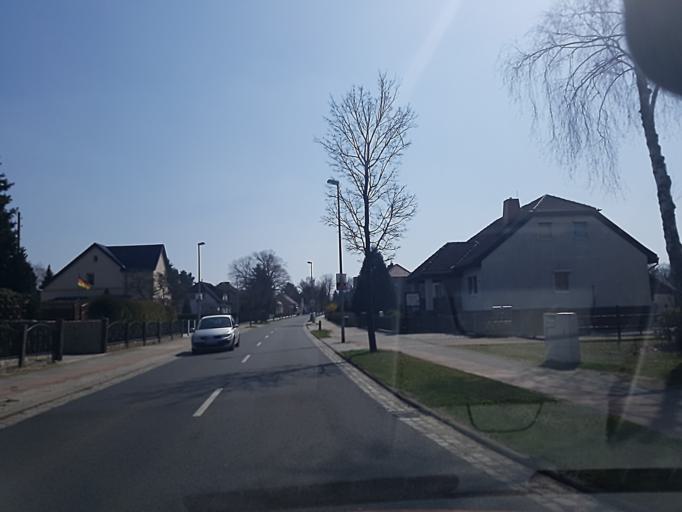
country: DE
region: Brandenburg
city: Tschernitz
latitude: 51.6112
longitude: 14.6052
